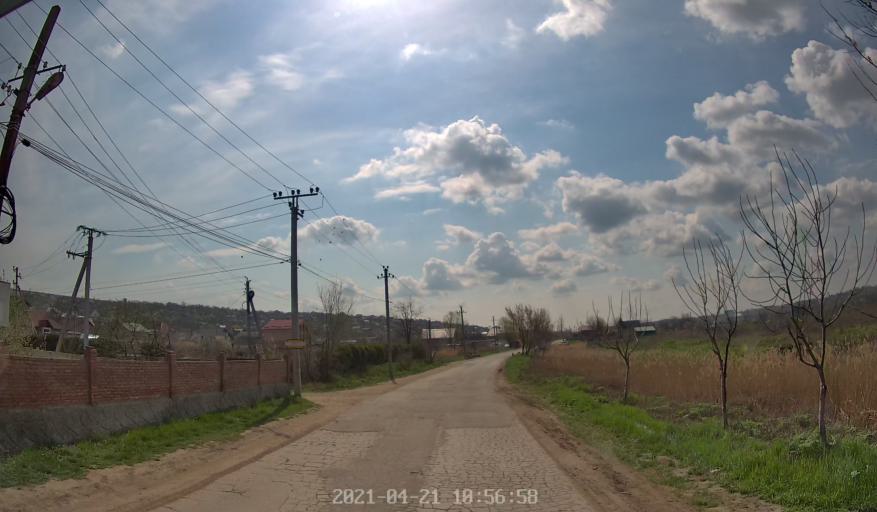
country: MD
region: Chisinau
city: Singera
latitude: 46.9623
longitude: 28.9375
